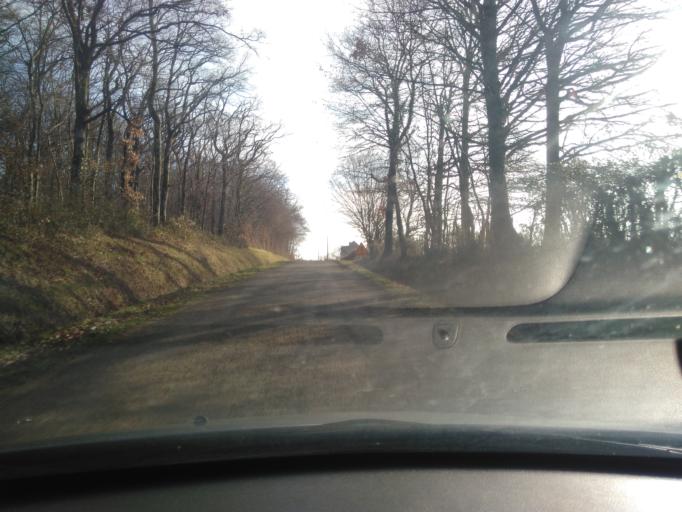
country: FR
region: Bourgogne
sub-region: Departement de la Nievre
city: Saint-Parize-le-Chatel
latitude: 46.8356
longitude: 3.2358
